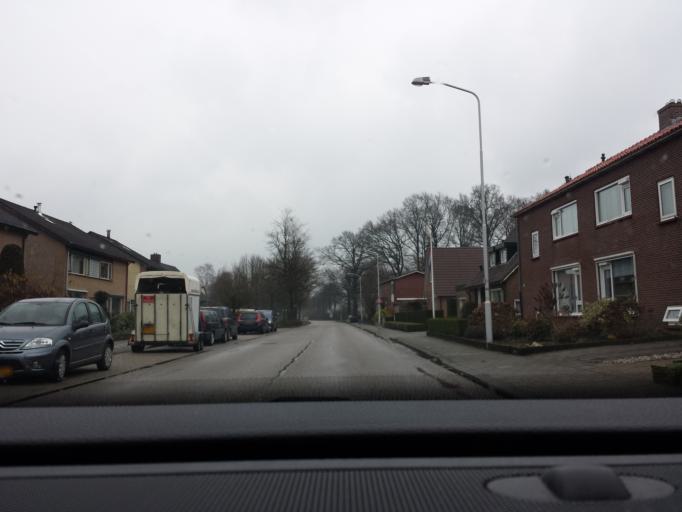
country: NL
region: Gelderland
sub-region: Oude IJsselstreek
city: Varsseveld
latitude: 51.9459
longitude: 6.4581
